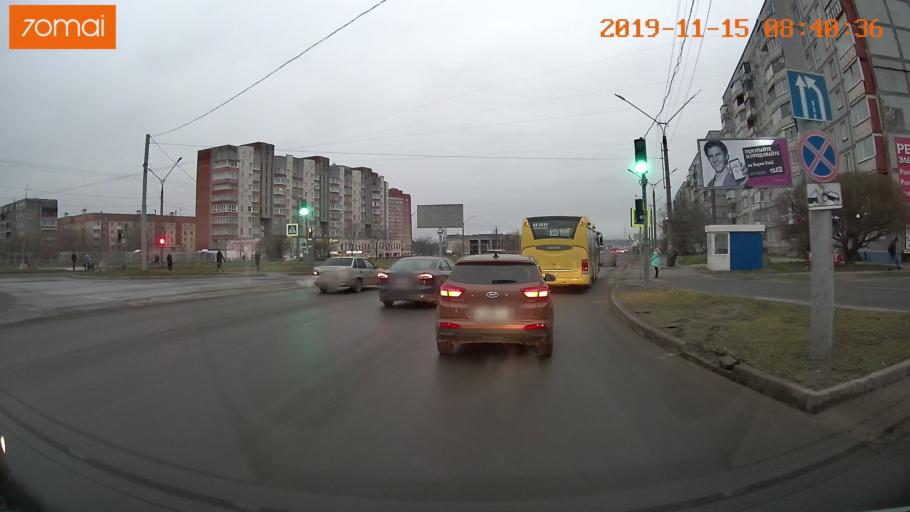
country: RU
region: Vologda
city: Cherepovets
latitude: 59.0949
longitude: 37.9139
